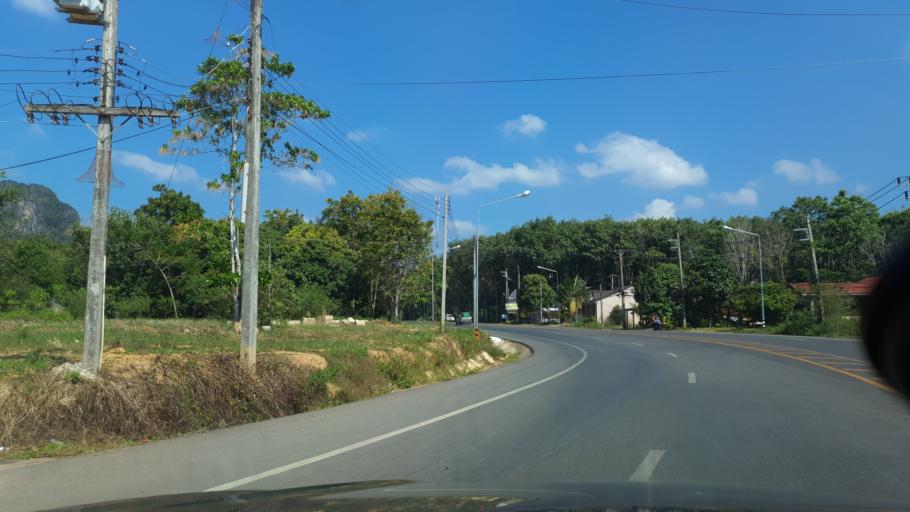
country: TH
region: Krabi
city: Krabi
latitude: 8.0693
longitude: 98.8590
